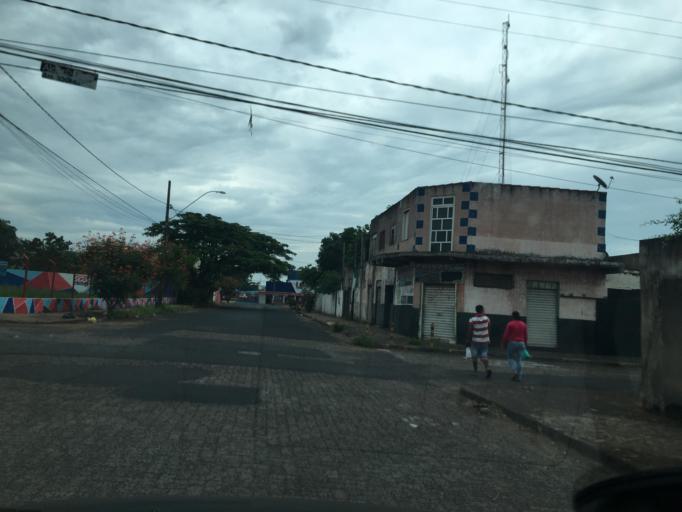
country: BR
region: Minas Gerais
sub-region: Uberlandia
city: Uberlandia
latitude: -18.9320
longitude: -48.3193
